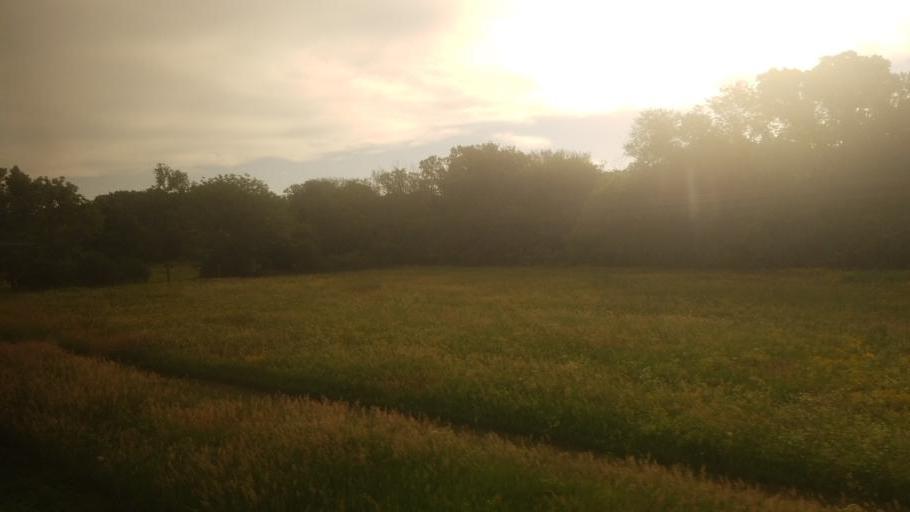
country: US
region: Kansas
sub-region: Osage County
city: Carbondale
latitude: 38.8730
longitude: -95.6887
